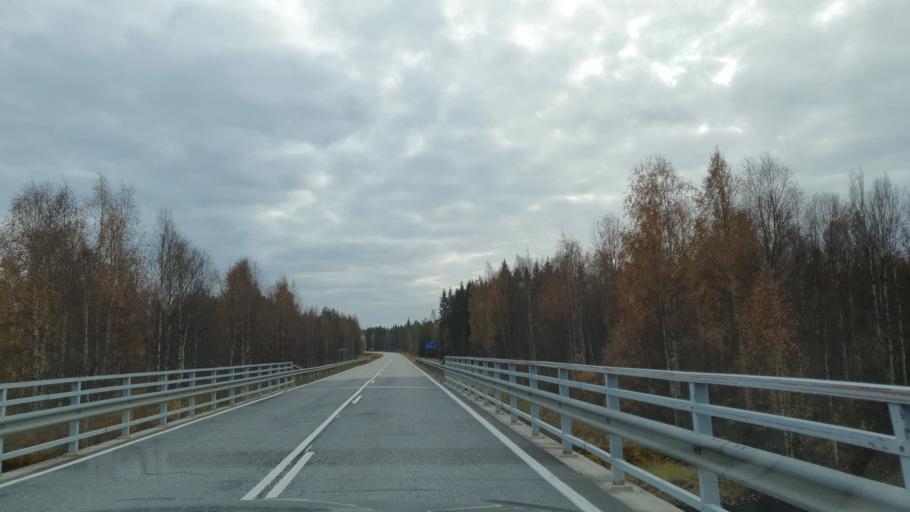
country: FI
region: Kainuu
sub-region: Kehys-Kainuu
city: Puolanka
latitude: 65.2465
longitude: 27.5795
